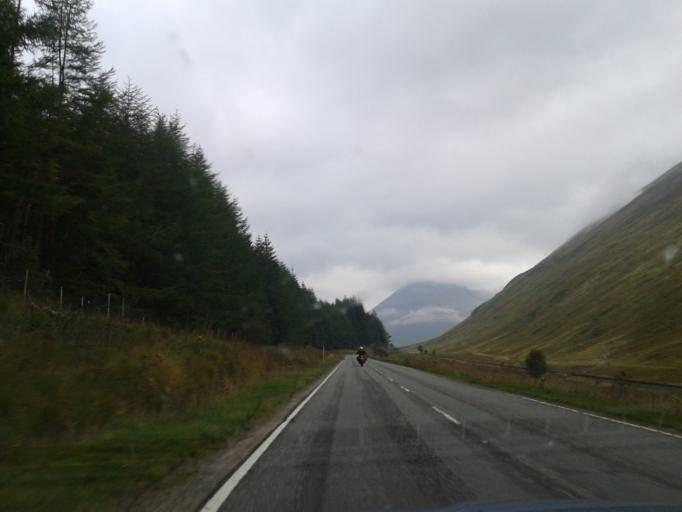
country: GB
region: Scotland
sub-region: Argyll and Bute
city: Garelochhead
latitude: 56.4521
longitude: -4.7108
